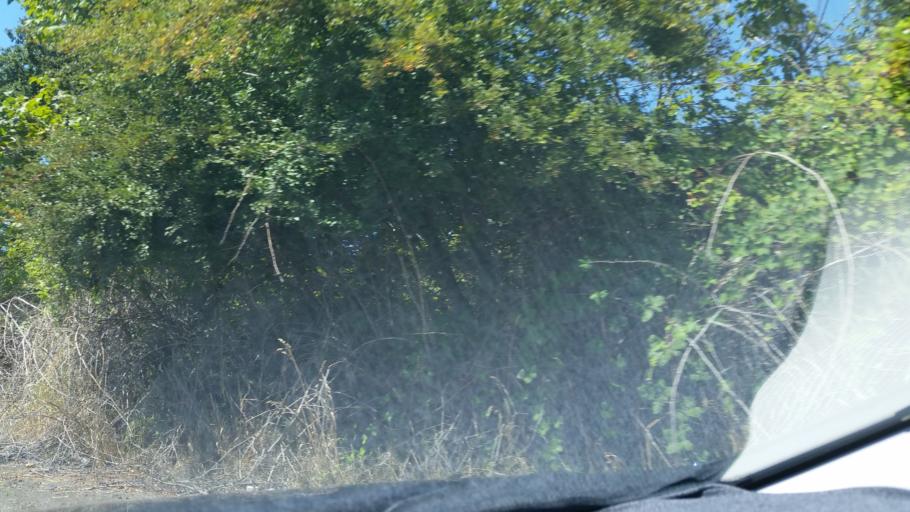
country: US
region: Oregon
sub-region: Clackamas County
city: Wilsonville
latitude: 45.2596
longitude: -122.7698
